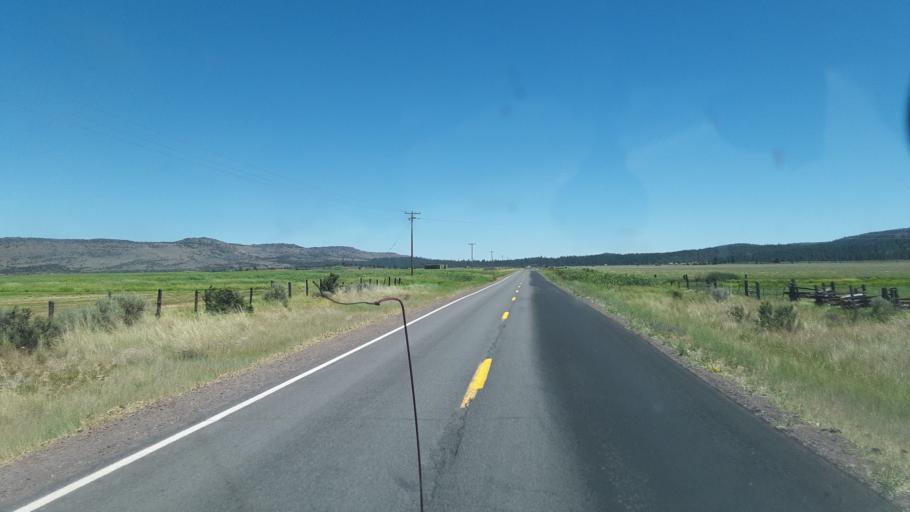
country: US
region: California
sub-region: Lassen County
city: Susanville
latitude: 40.5377
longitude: -120.6163
